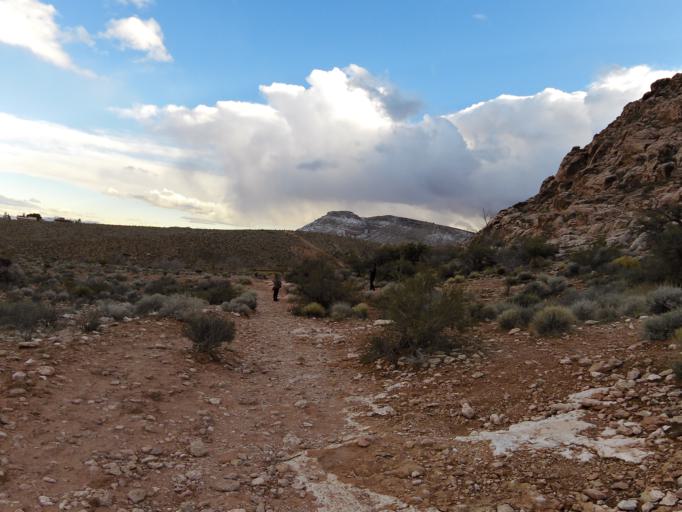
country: US
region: Nevada
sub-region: Clark County
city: Summerlin South
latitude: 36.1480
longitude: -115.4217
